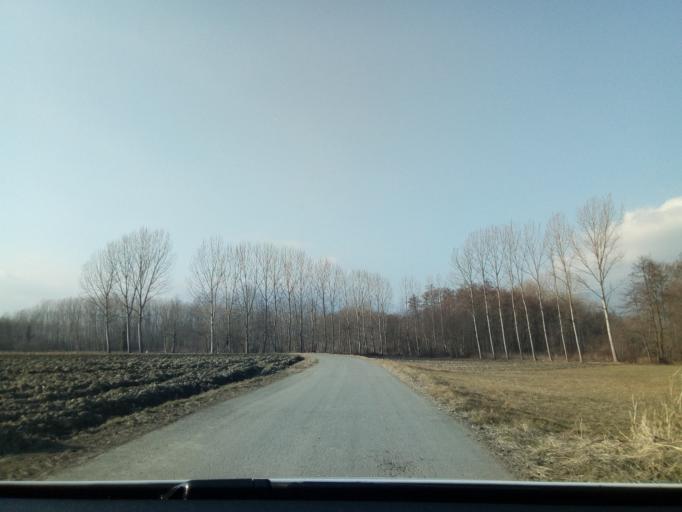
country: IT
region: Piedmont
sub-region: Provincia di Torino
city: Bollengo
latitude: 45.4530
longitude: 7.9355
